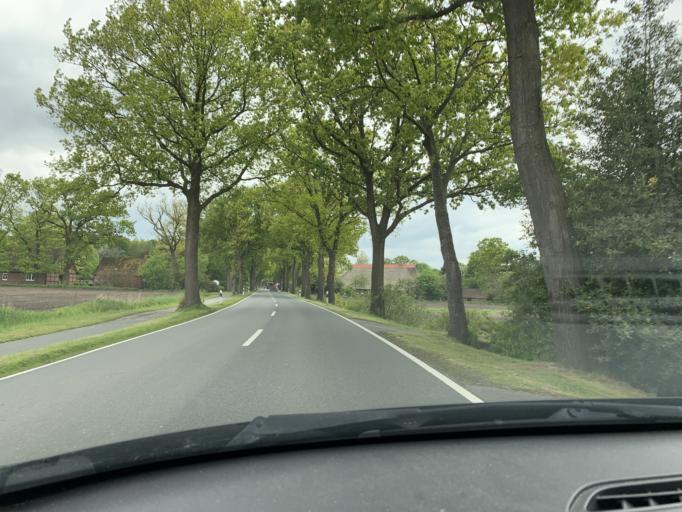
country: DE
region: Lower Saxony
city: Westerstede
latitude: 53.2439
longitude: 7.9213
